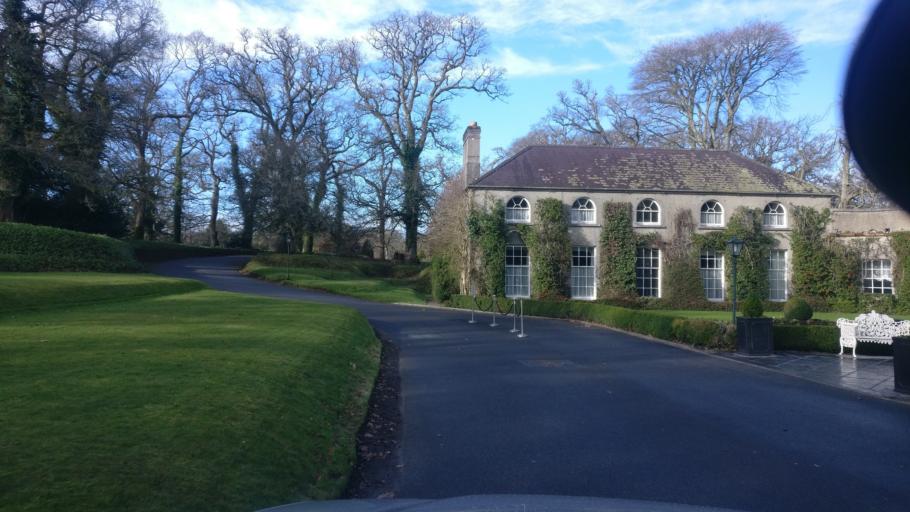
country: IE
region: Leinster
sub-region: Kilkenny
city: Thomastown
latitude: 52.5293
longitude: -7.1882
